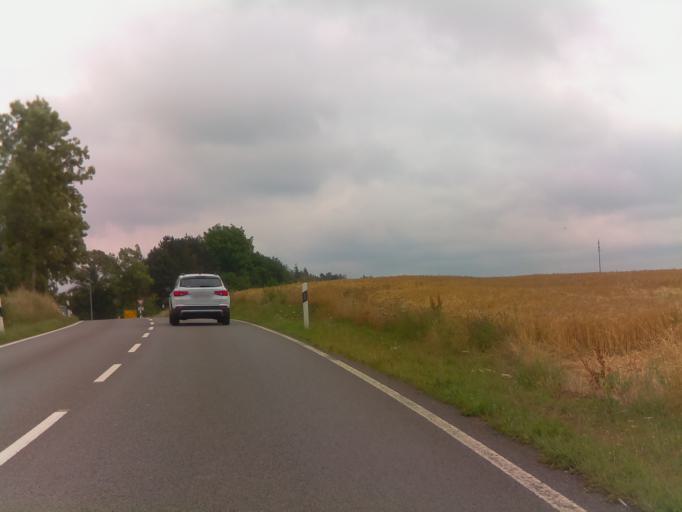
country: LU
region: Luxembourg
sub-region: Canton de Capellen
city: Koerich
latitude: 49.6487
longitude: 5.9448
